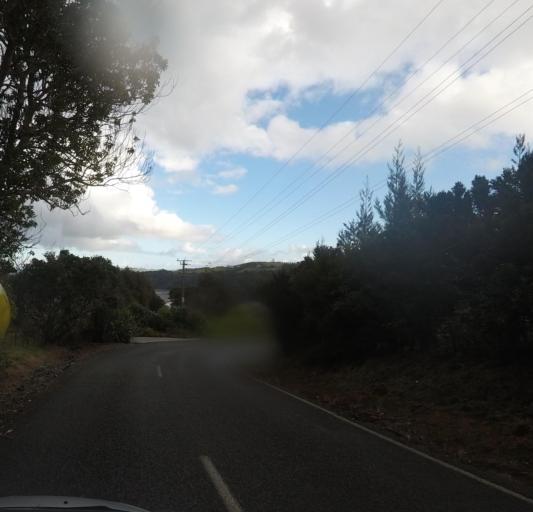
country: NZ
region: Auckland
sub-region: Auckland
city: Warkworth
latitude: -36.3790
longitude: 174.7590
